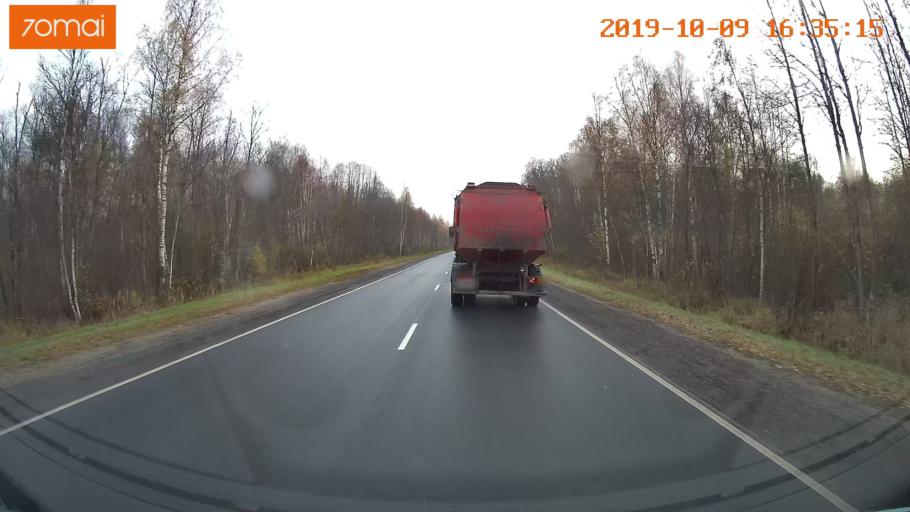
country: RU
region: Kostroma
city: Oktyabr'skiy
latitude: 57.5577
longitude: 40.9991
